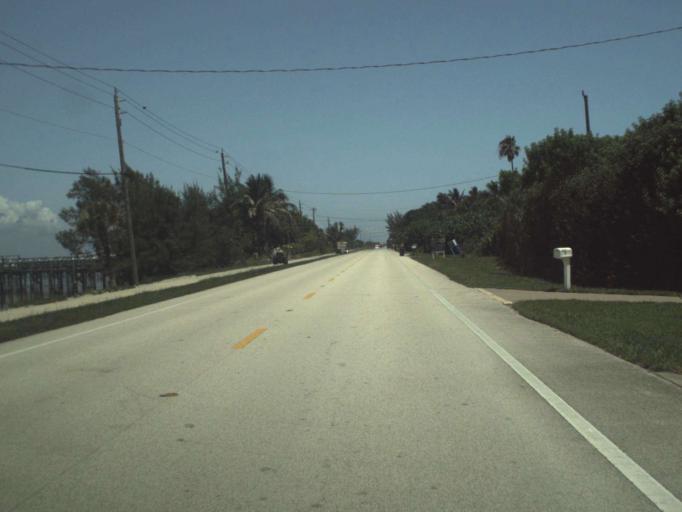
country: US
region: Florida
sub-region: Indian River County
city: Sebastian
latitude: 27.8284
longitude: -80.4317
